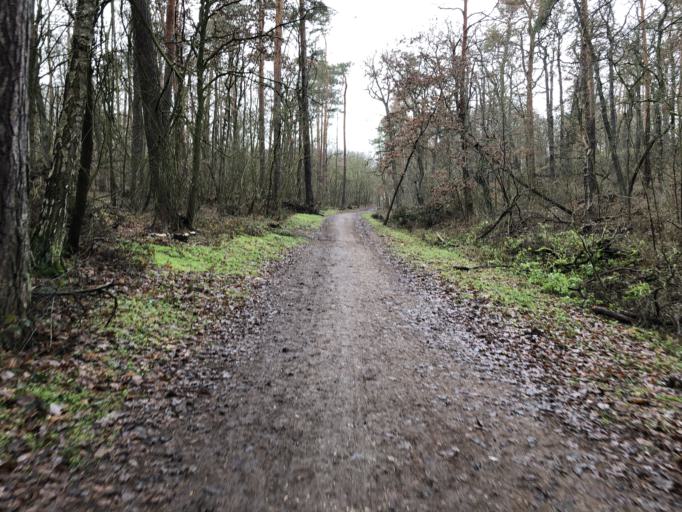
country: DE
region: Saxony-Anhalt
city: Halle Neustadt
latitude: 51.5047
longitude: 11.9080
